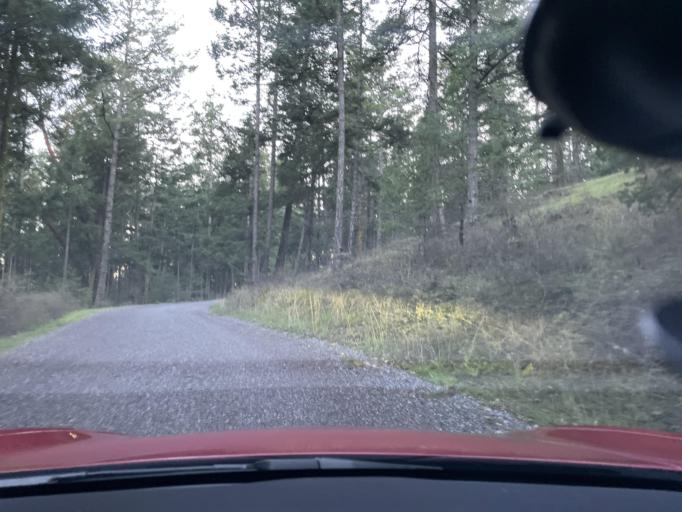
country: US
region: Washington
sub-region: San Juan County
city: Friday Harbor
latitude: 48.6137
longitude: -123.1471
